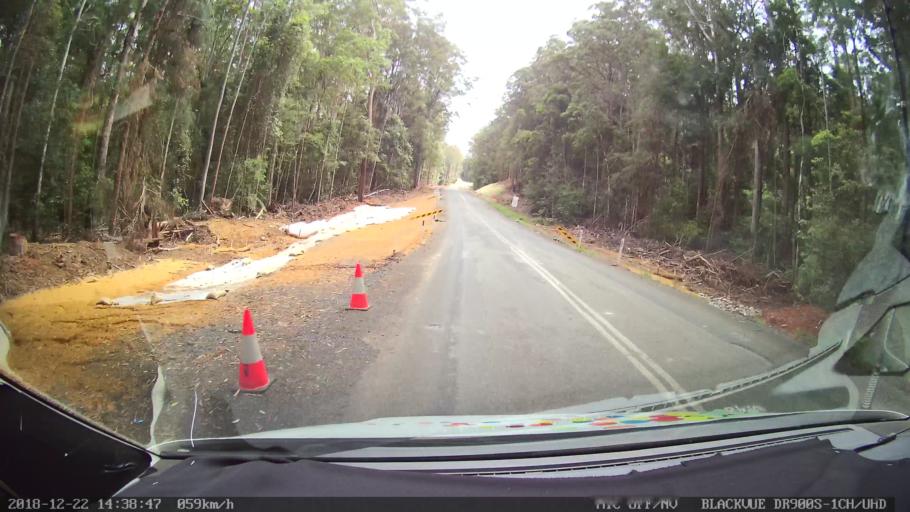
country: AU
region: New South Wales
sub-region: Bellingen
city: Dorrigo
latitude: -30.1409
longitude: 152.5954
